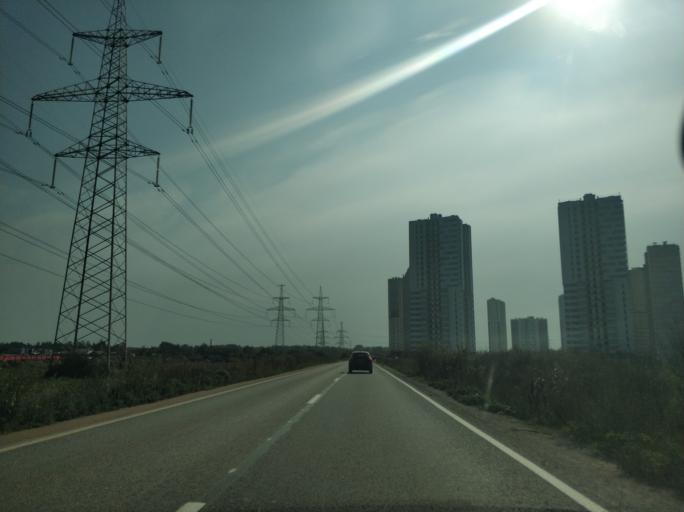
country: RU
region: St.-Petersburg
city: Krasnogvargeisky
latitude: 60.0140
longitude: 30.4788
